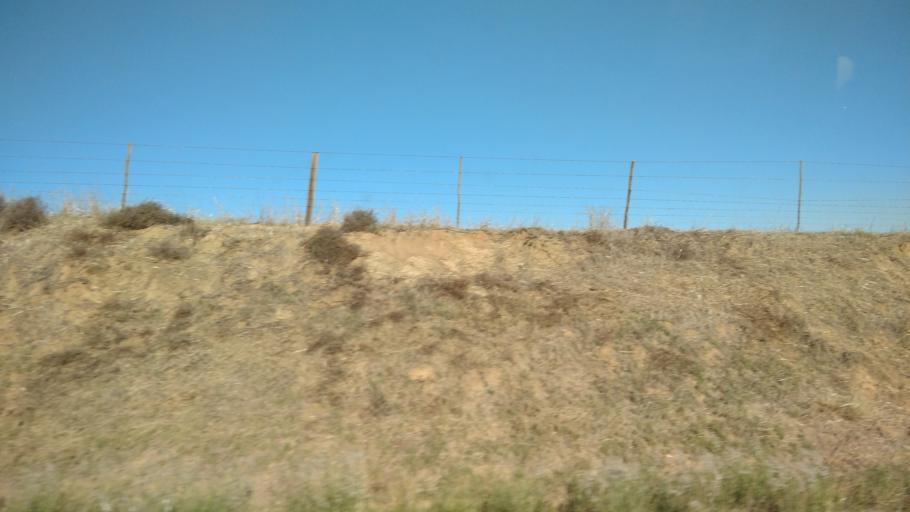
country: ZA
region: Western Cape
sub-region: West Coast District Municipality
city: Malmesbury
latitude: -33.3863
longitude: 18.6707
